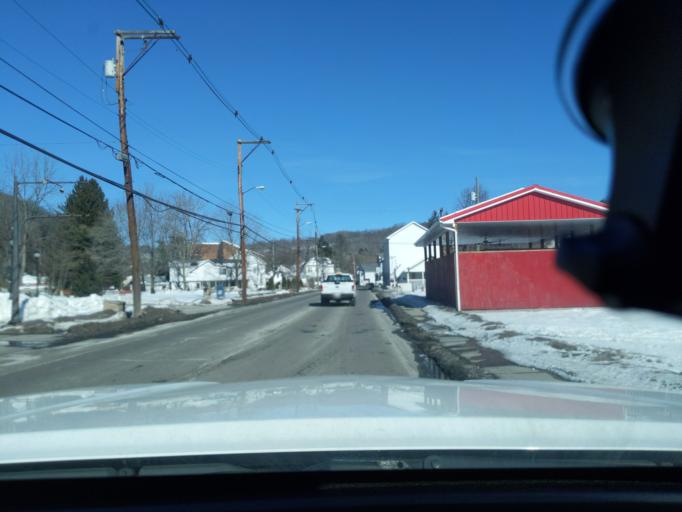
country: US
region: Maryland
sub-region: Allegany County
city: Lonaconing
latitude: 39.5692
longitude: -78.9779
